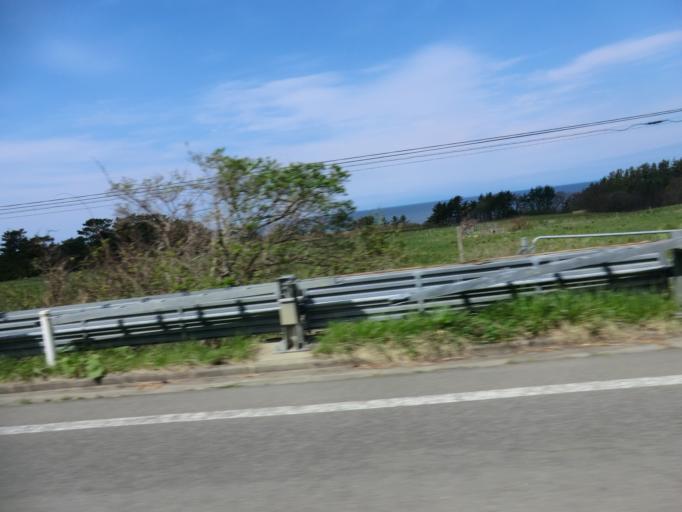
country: JP
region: Hokkaido
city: Hakodate
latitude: 41.4626
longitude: 140.8861
